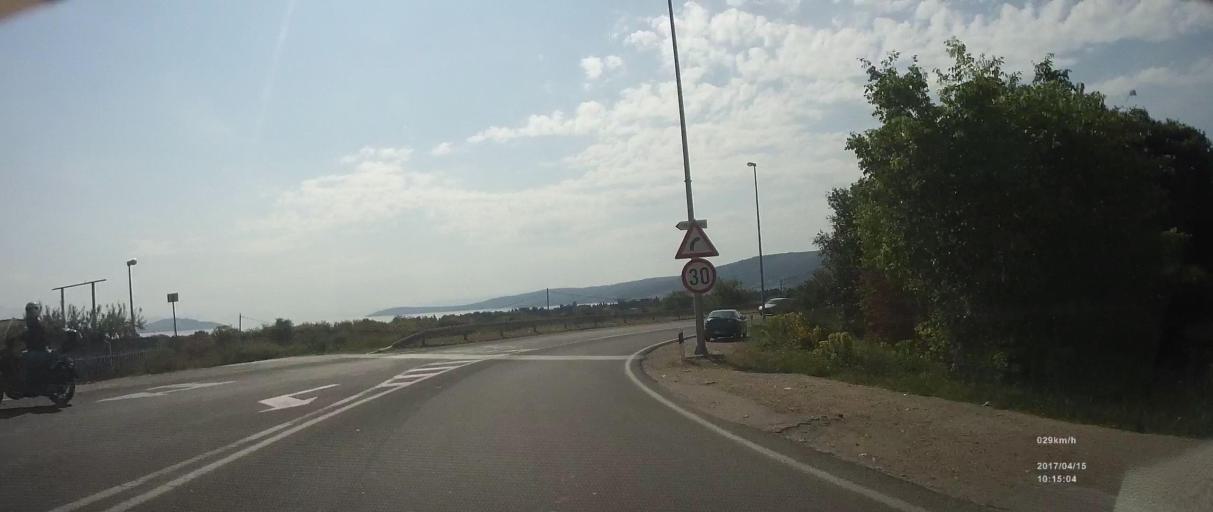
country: HR
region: Splitsko-Dalmatinska
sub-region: Grad Trogir
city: Trogir
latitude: 43.5366
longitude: 16.2864
